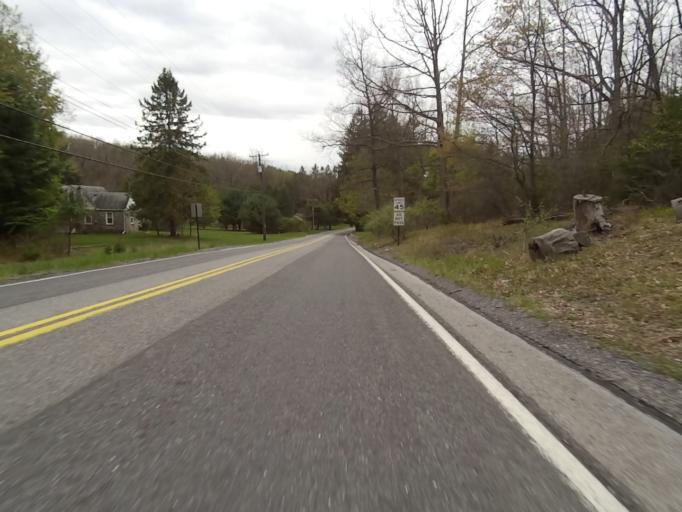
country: US
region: Pennsylvania
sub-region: Clearfield County
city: Troy
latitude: 40.9008
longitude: -78.1373
